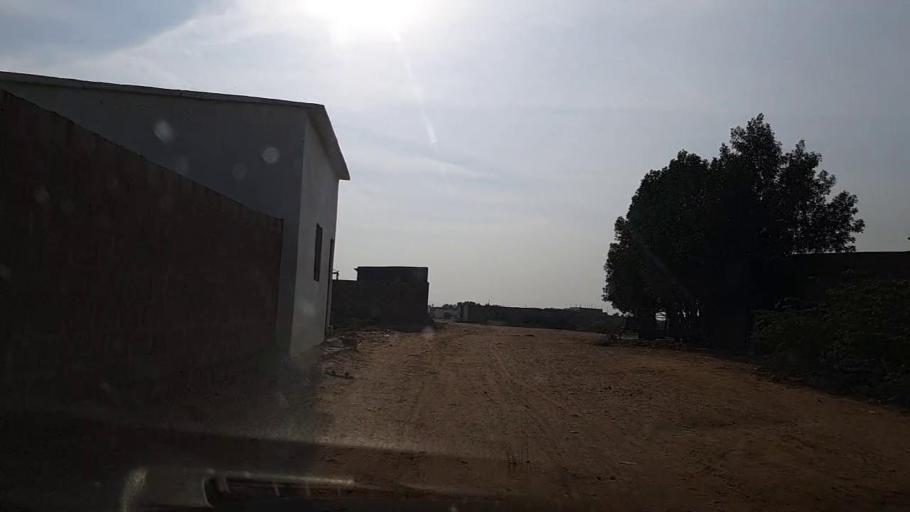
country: PK
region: Sindh
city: Gharo
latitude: 24.7956
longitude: 67.5351
